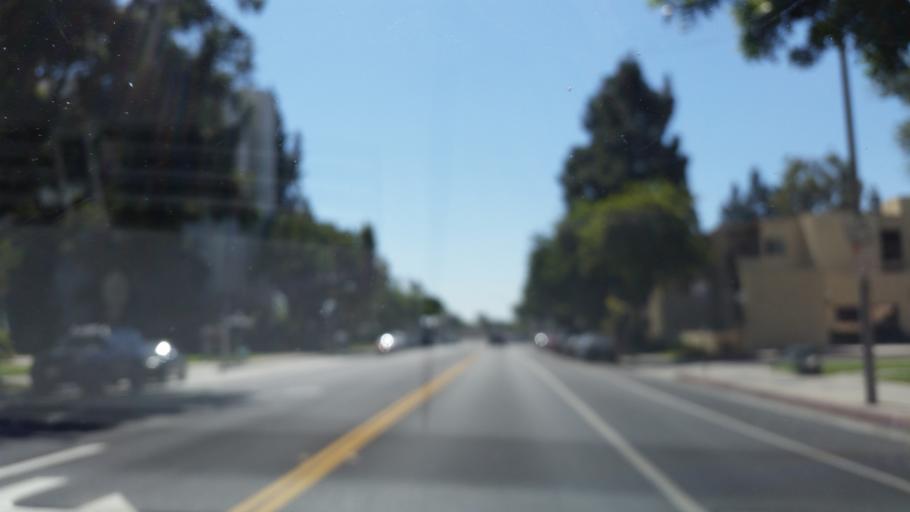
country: US
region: California
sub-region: Orange County
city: Santa Ana
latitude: 33.7469
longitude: -117.8725
